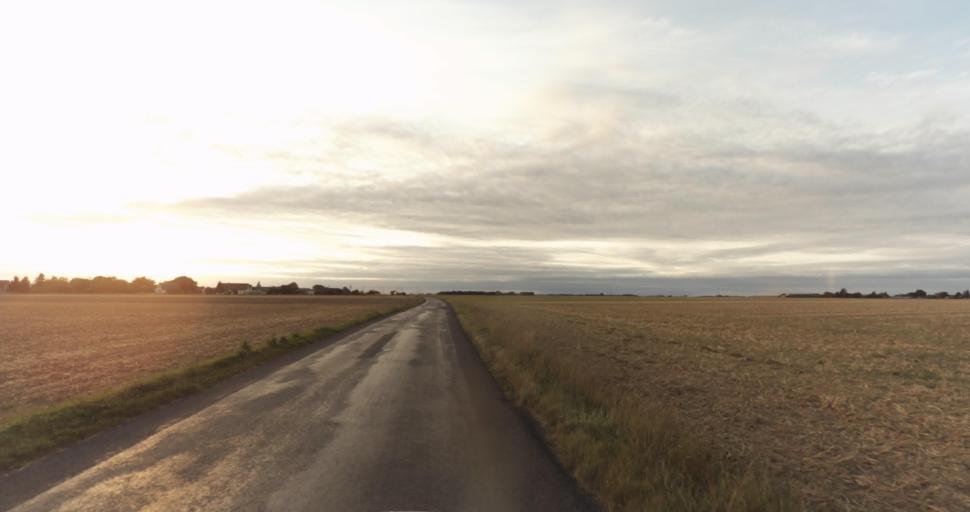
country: FR
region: Haute-Normandie
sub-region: Departement de l'Eure
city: La Madeleine-de-Nonancourt
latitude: 48.8697
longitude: 1.2220
